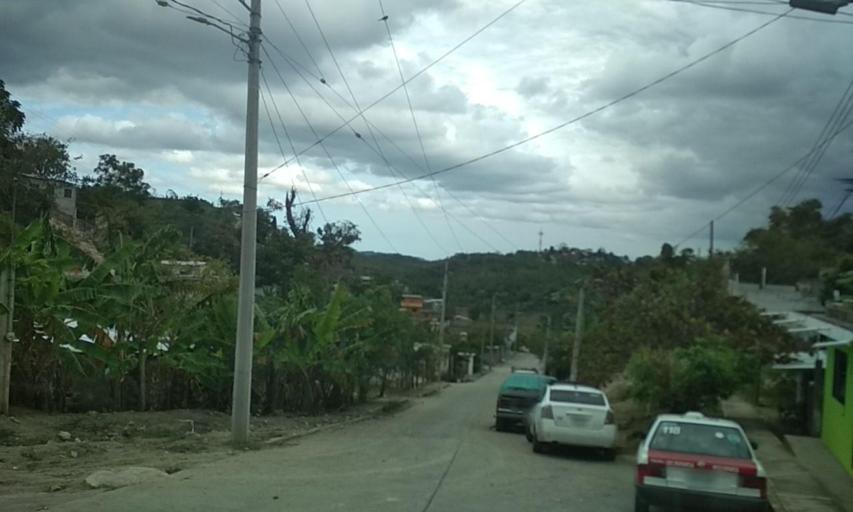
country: MX
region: Veracruz
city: Papantla de Olarte
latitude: 20.4576
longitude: -97.3160
